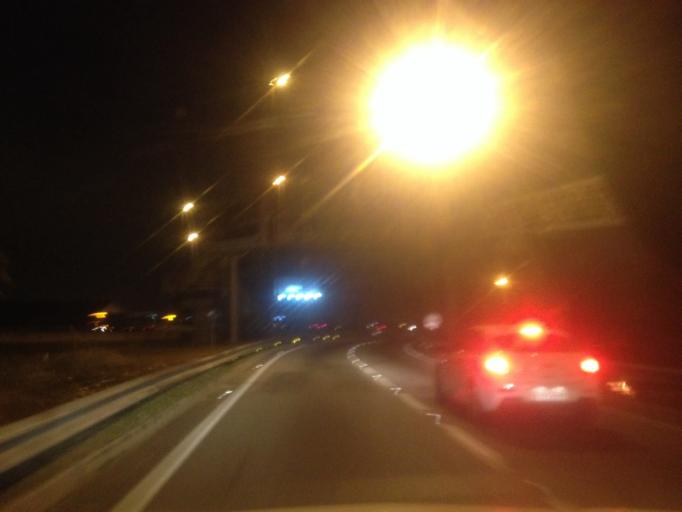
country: BR
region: Rio de Janeiro
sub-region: Sao Joao De Meriti
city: Sao Joao de Meriti
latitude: -22.8033
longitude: -43.3469
